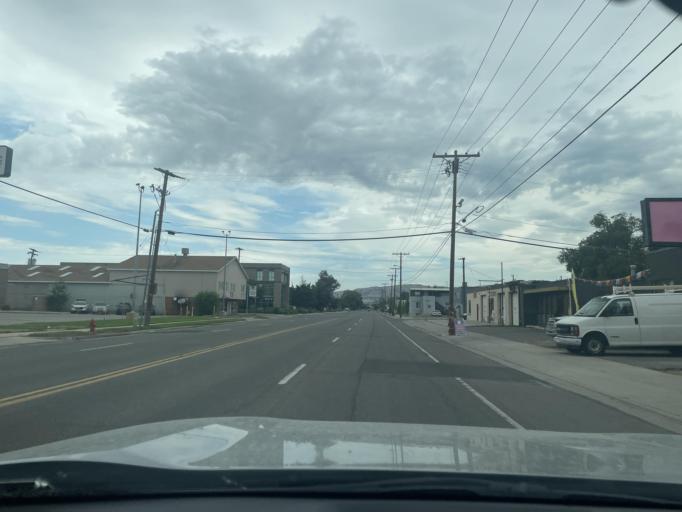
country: US
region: Utah
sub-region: Salt Lake County
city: Centerfield
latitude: 40.7019
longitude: -111.8911
